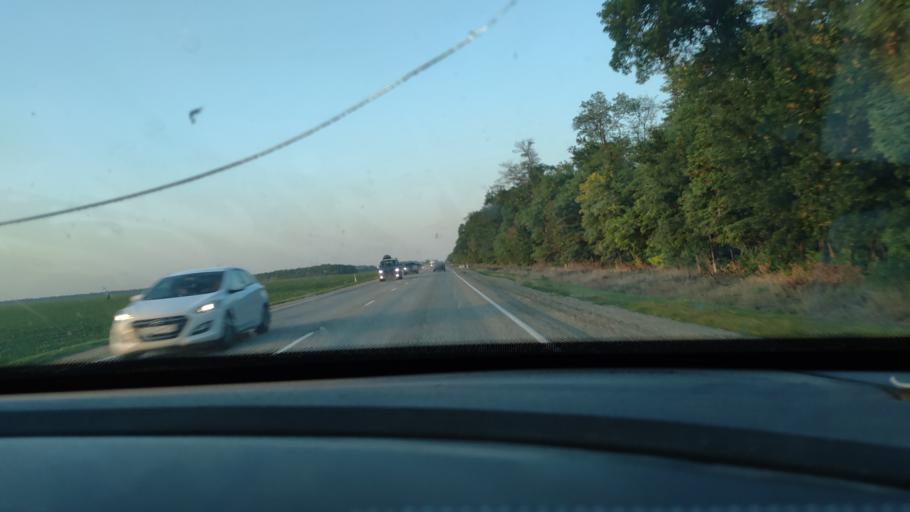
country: RU
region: Krasnodarskiy
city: Starominskaya
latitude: 46.4558
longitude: 39.0336
